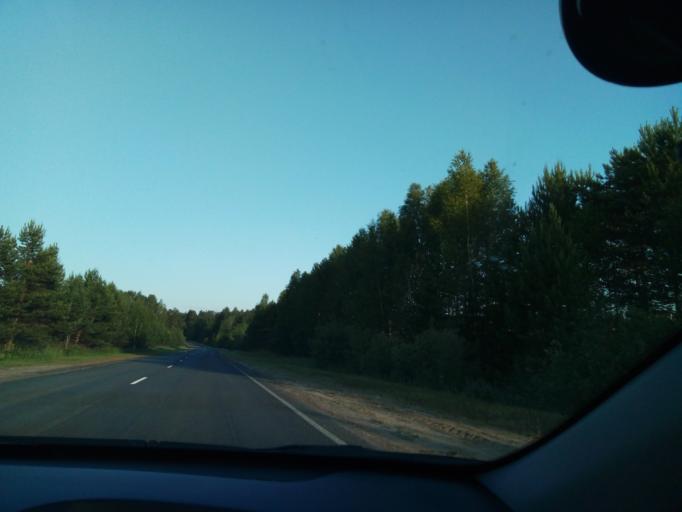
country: RU
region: Nizjnij Novgorod
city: Satis
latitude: 54.9352
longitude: 43.2278
